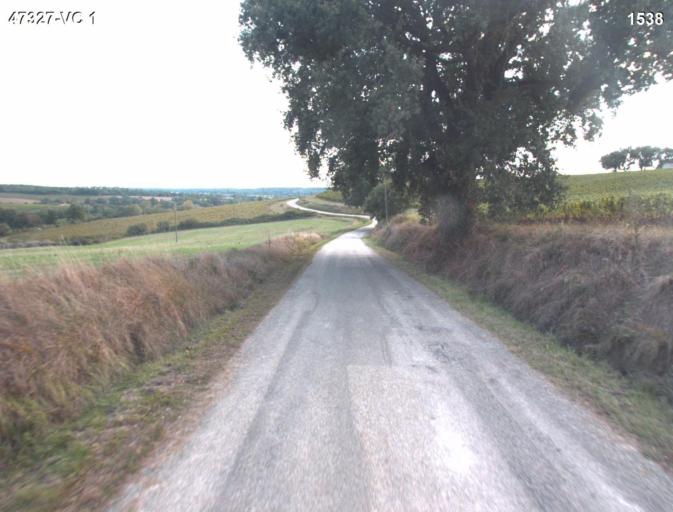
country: FR
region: Aquitaine
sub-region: Departement du Lot-et-Garonne
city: Barbaste
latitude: 44.1983
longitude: 0.2578
